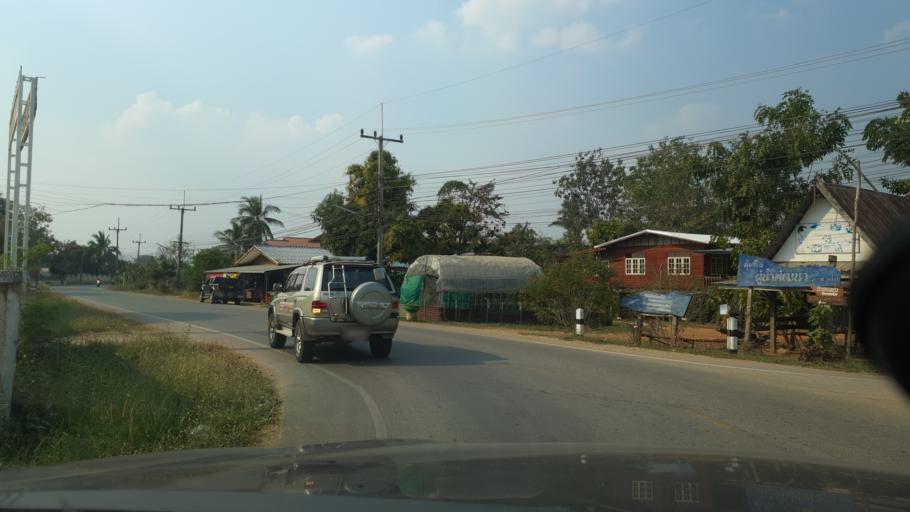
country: TH
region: Sukhothai
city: Ban Dan Lan Hoi
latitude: 17.1127
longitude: 99.5499
